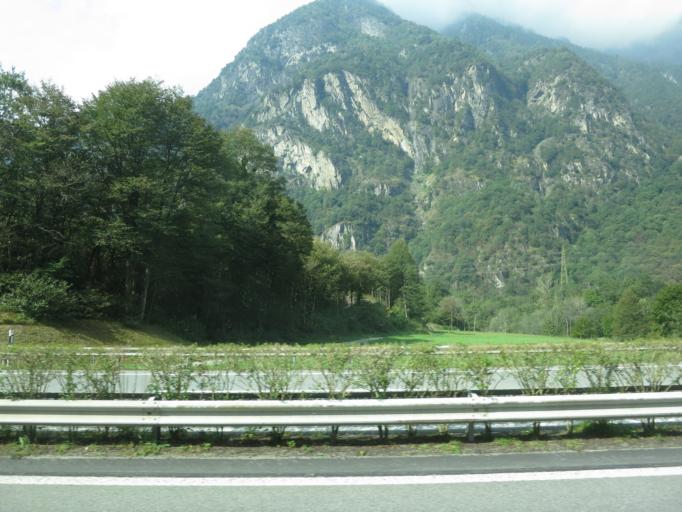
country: CH
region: Grisons
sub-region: Moesa District
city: Santa Maria in Calanca
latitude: 46.2849
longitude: 9.1802
